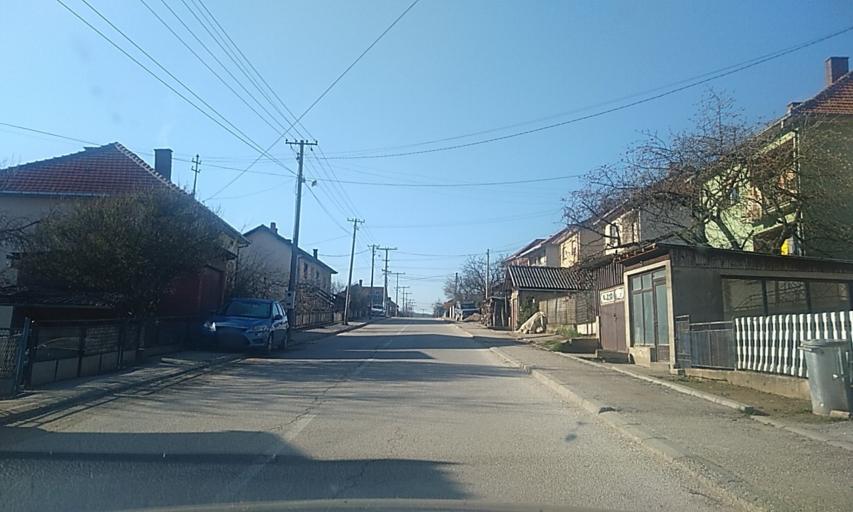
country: RS
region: Central Serbia
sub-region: Pcinjski Okrug
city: Bosilegrad
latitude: 42.4946
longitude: 22.4701
